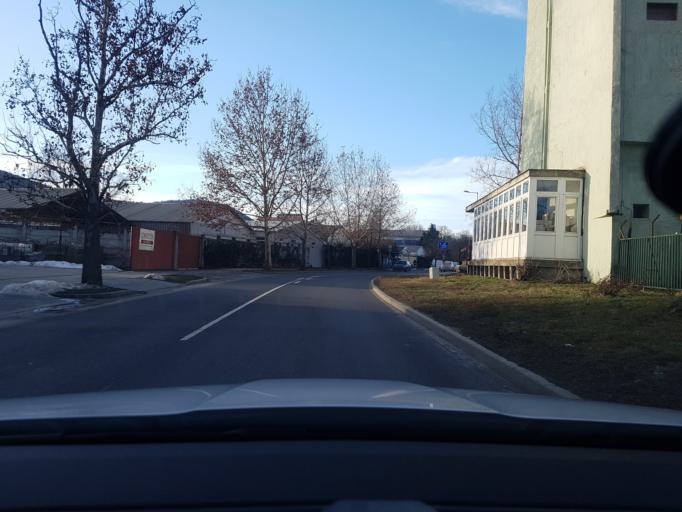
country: HU
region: Budapest
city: Budapest III. keruelet
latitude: 47.5676
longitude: 19.0288
